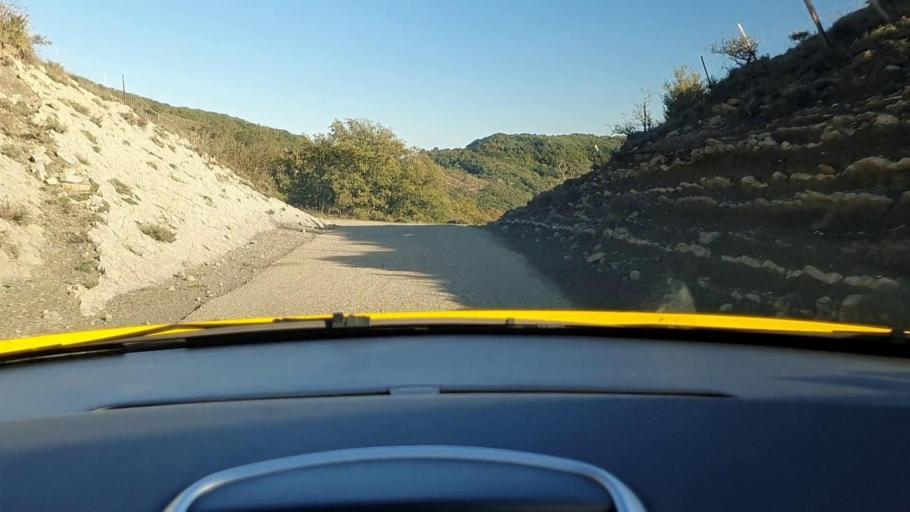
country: FR
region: Languedoc-Roussillon
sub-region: Departement du Gard
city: Sumene
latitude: 43.9767
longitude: 3.7529
